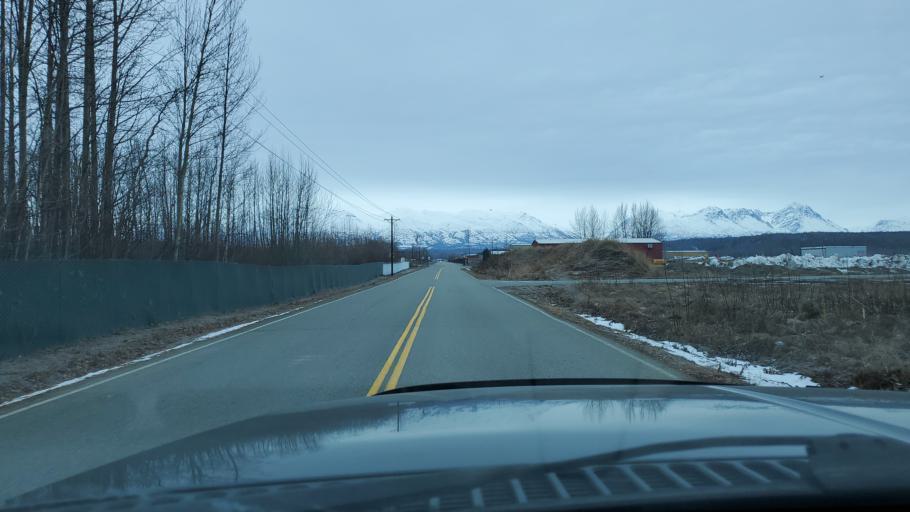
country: US
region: Alaska
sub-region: Matanuska-Susitna Borough
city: Palmer
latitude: 61.5975
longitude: -149.0951
